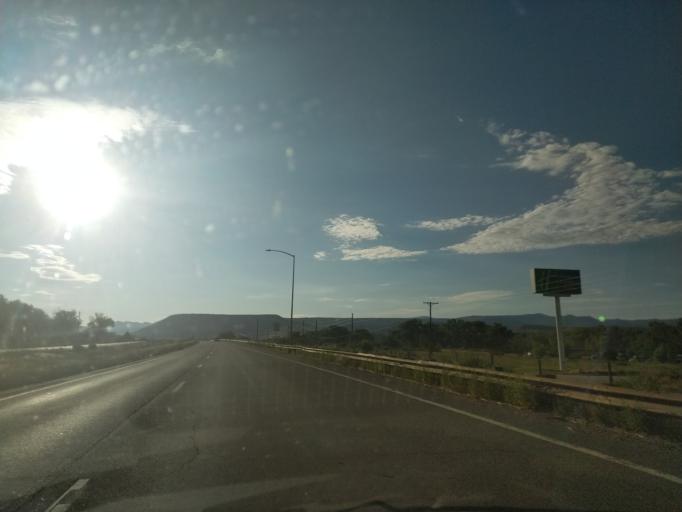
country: US
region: Colorado
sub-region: Garfield County
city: Silt
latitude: 39.5441
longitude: -107.6487
